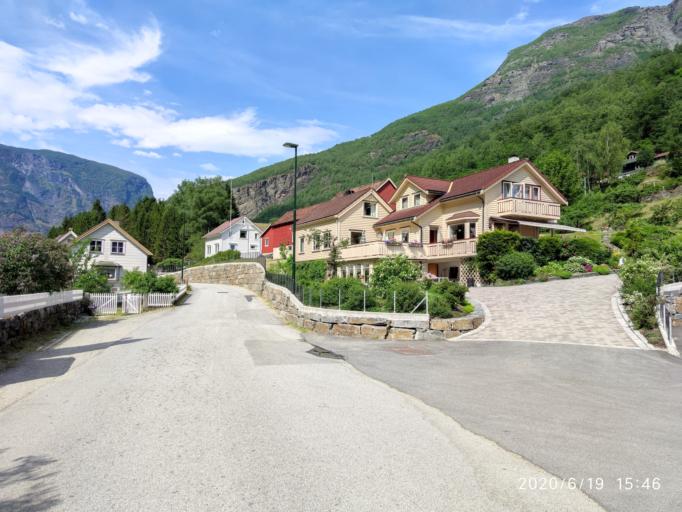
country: NO
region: Sogn og Fjordane
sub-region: Aurland
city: Aurlandsvangen
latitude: 60.8376
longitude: 7.1218
